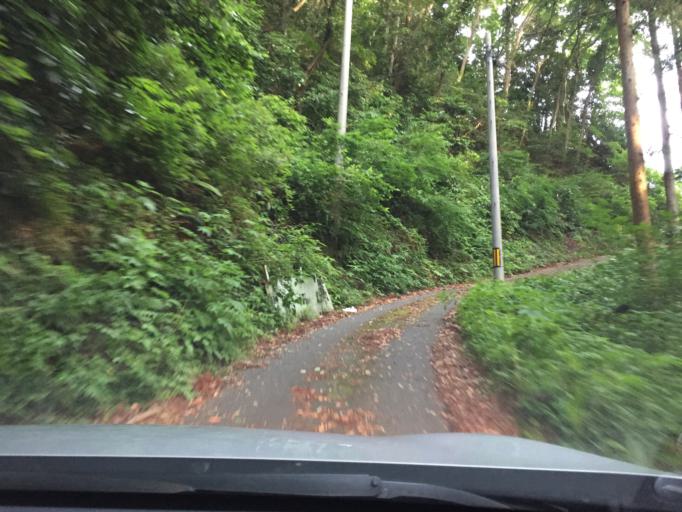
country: JP
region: Fukushima
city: Iwaki
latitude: 37.0470
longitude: 140.9149
